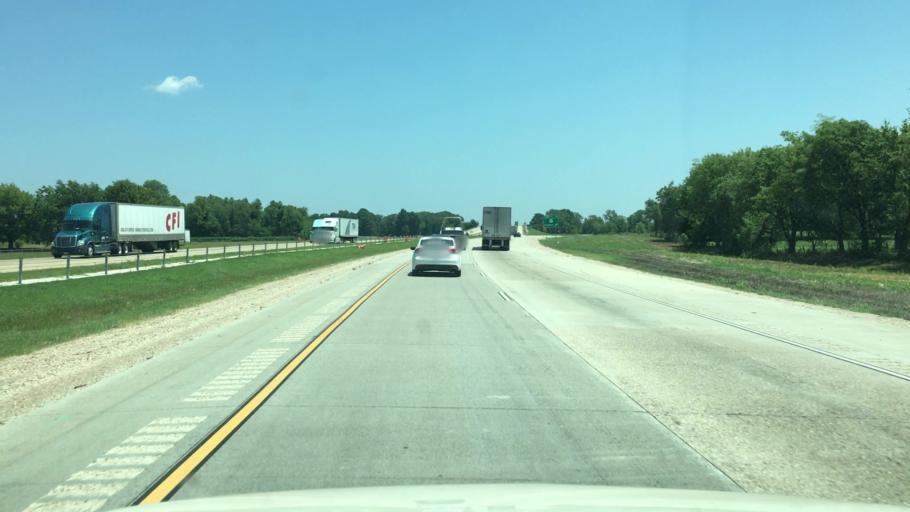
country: US
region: Arkansas
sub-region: Miller County
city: Texarkana
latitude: 33.5481
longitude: -93.8822
